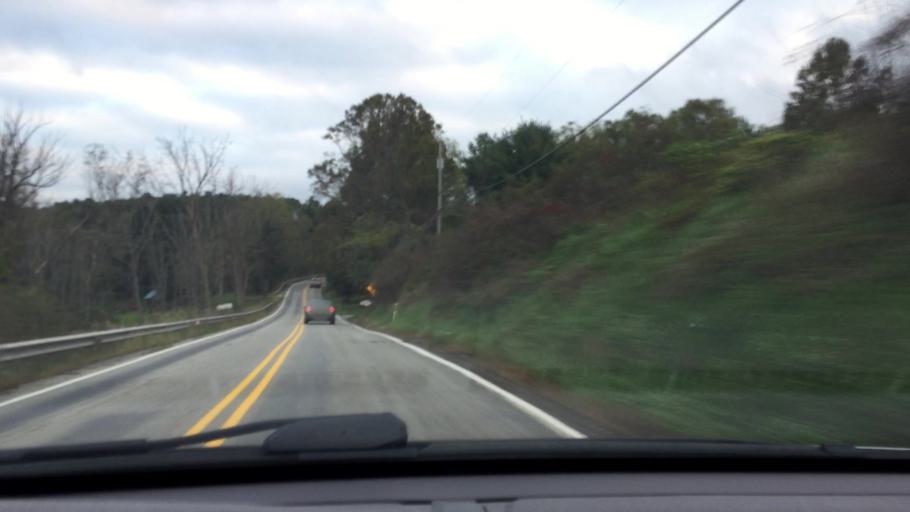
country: US
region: Pennsylvania
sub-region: Washington County
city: McMurray
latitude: 40.1835
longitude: -80.1001
